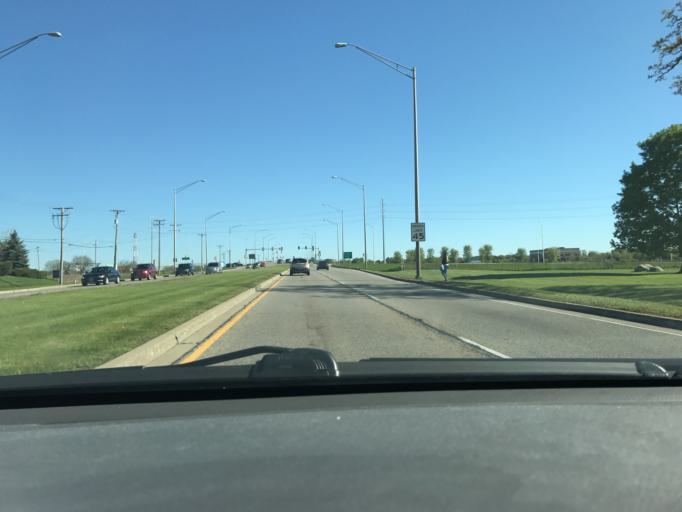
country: US
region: Illinois
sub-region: Kane County
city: Sleepy Hollow
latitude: 42.0770
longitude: -88.3355
